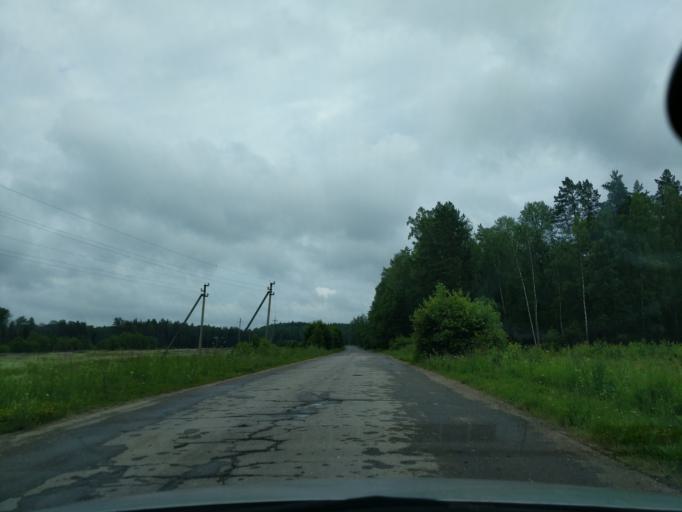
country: RU
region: Kaluga
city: Myatlevo
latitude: 54.8094
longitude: 35.6841
